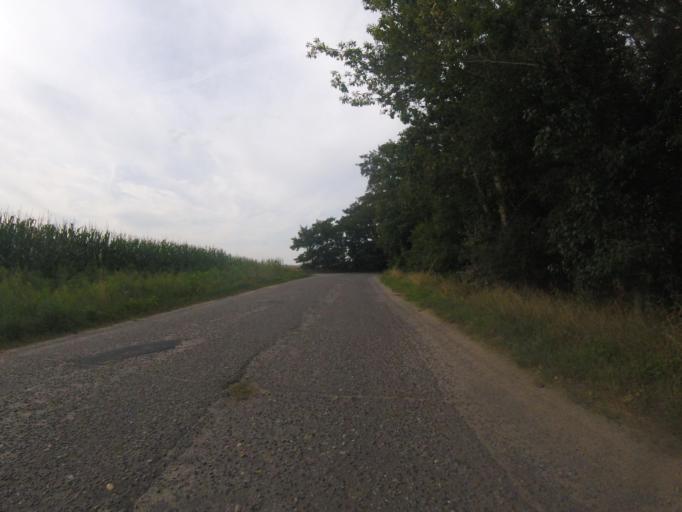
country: DE
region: Brandenburg
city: Rangsdorf
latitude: 52.2972
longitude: 13.4762
